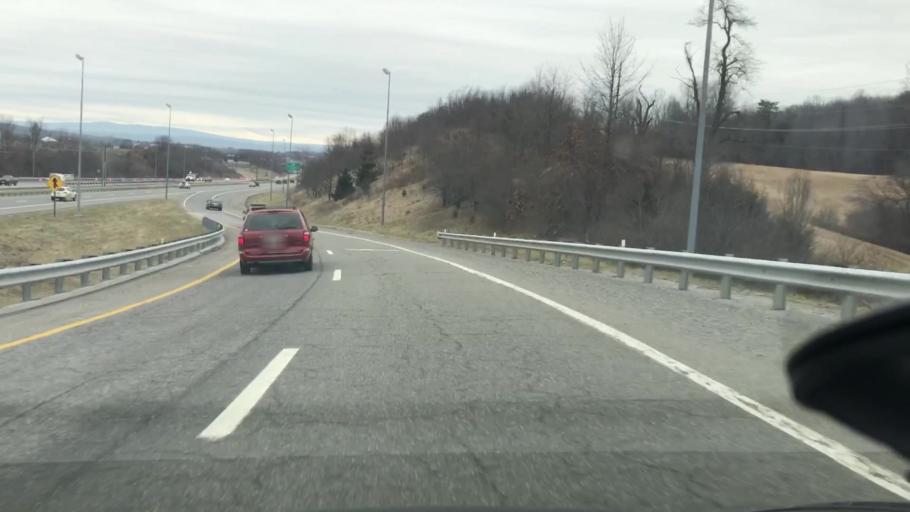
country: US
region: Virginia
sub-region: Montgomery County
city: Christiansburg
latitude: 37.1570
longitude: -80.4120
